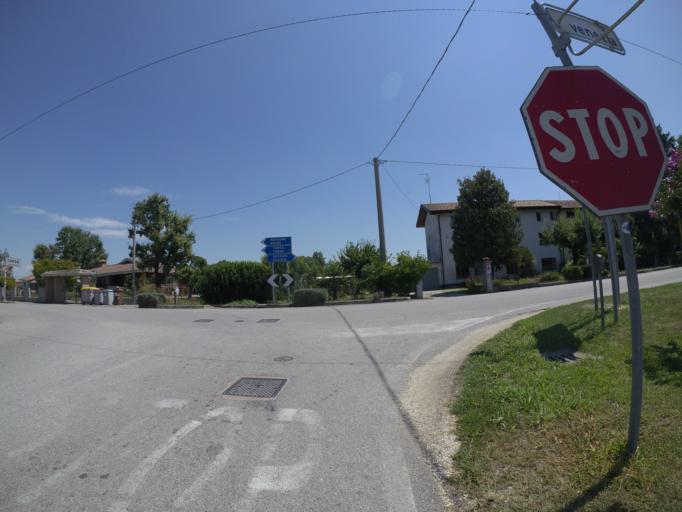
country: IT
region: Friuli Venezia Giulia
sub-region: Provincia di Udine
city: Pocenia
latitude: 45.8673
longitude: 13.1104
